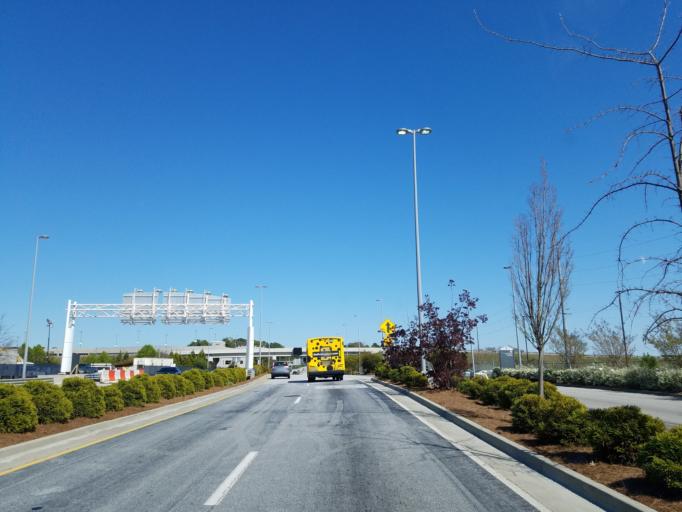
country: US
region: Georgia
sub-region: Fulton County
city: Hapeville
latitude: 33.6409
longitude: -84.4077
